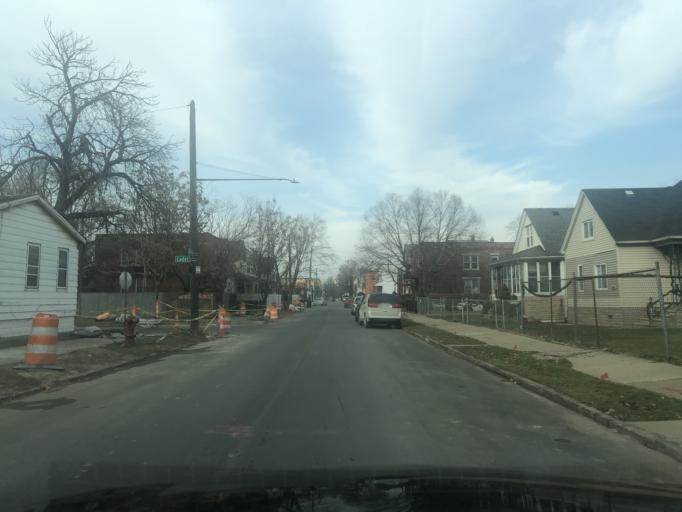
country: US
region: Michigan
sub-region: Wayne County
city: River Rouge
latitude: 42.3150
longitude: -83.1047
